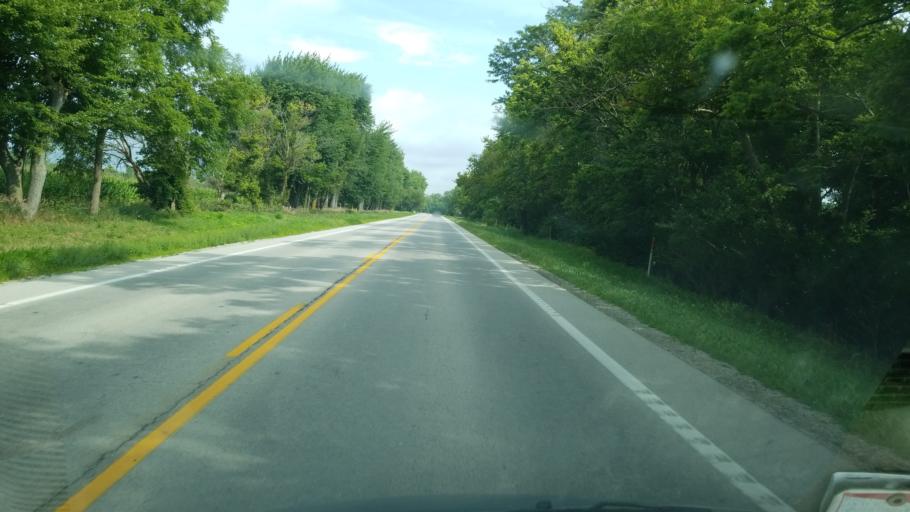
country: US
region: Ohio
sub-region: Sandusky County
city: Ballville
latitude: 41.2727
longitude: -83.1685
